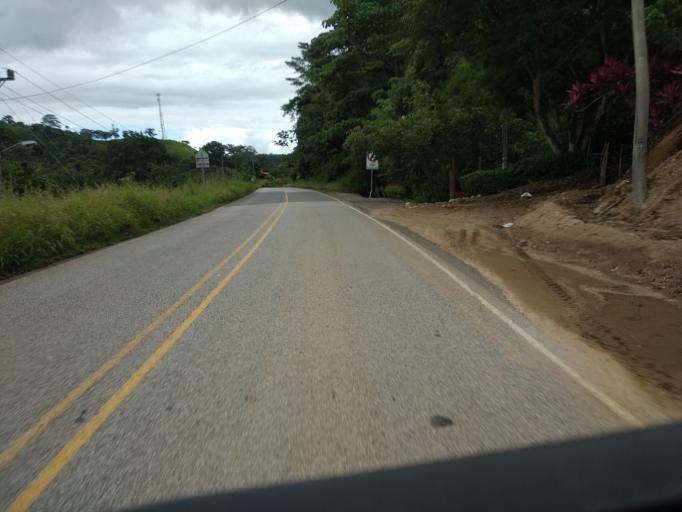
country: CR
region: Puntarenas
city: Buenos Aires
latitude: 9.1001
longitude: -83.2813
